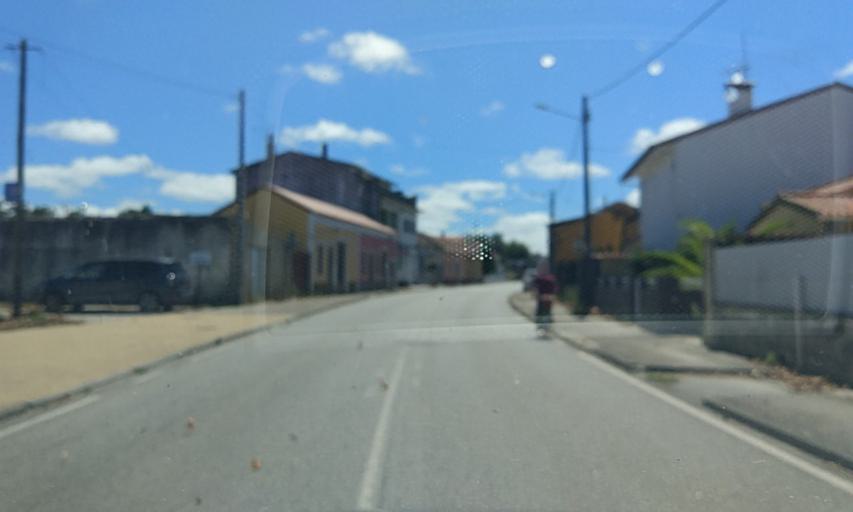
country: PT
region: Coimbra
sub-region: Mira
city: Mira
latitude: 40.4407
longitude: -8.7279
